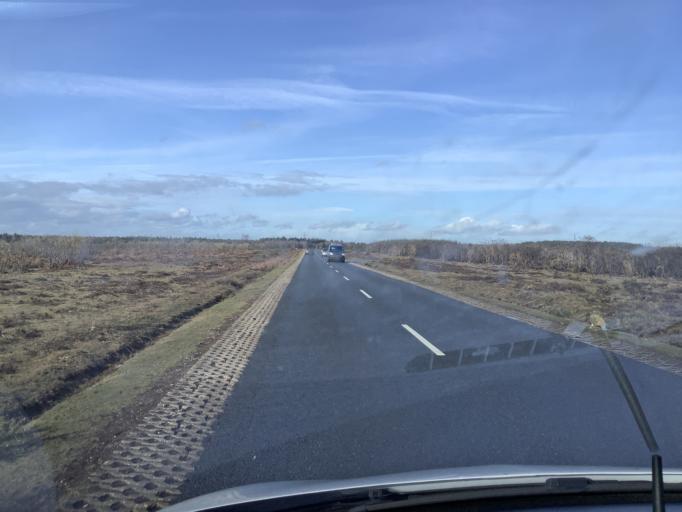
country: GB
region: England
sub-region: Hampshire
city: Hythe
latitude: 50.8351
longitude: -1.4286
